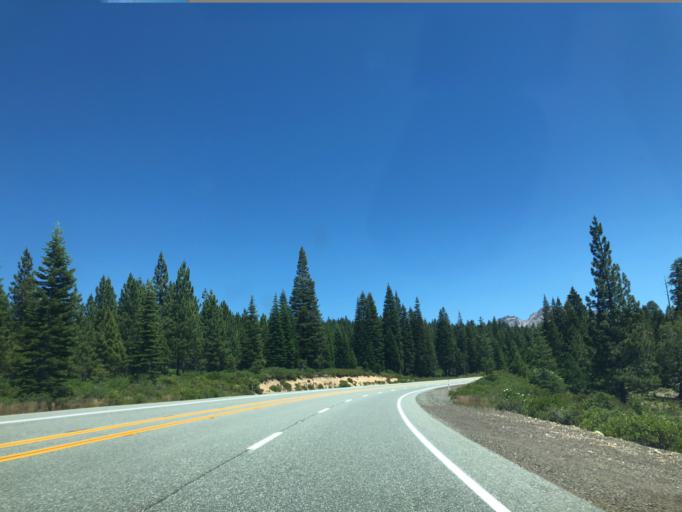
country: US
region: California
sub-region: Shasta County
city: Shingletown
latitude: 40.5419
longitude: -121.6041
